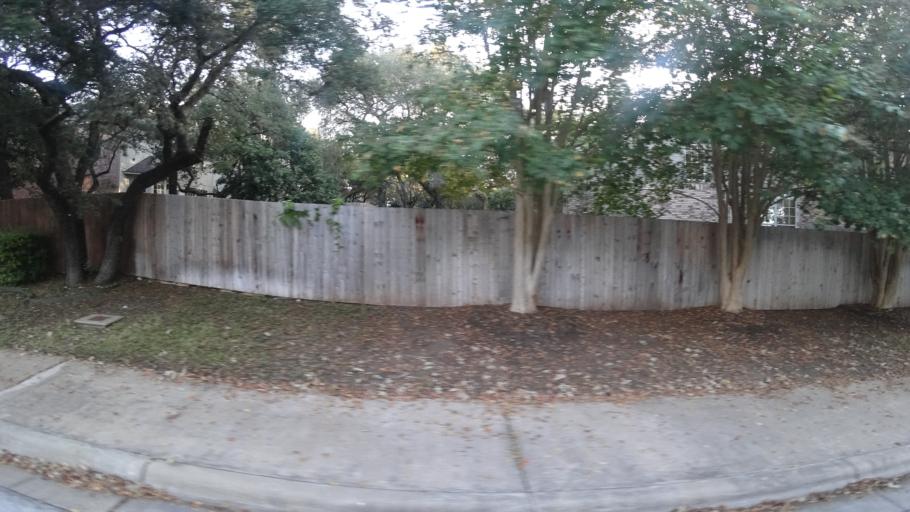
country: US
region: Texas
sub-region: Travis County
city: Hudson Bend
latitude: 30.3786
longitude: -97.8928
